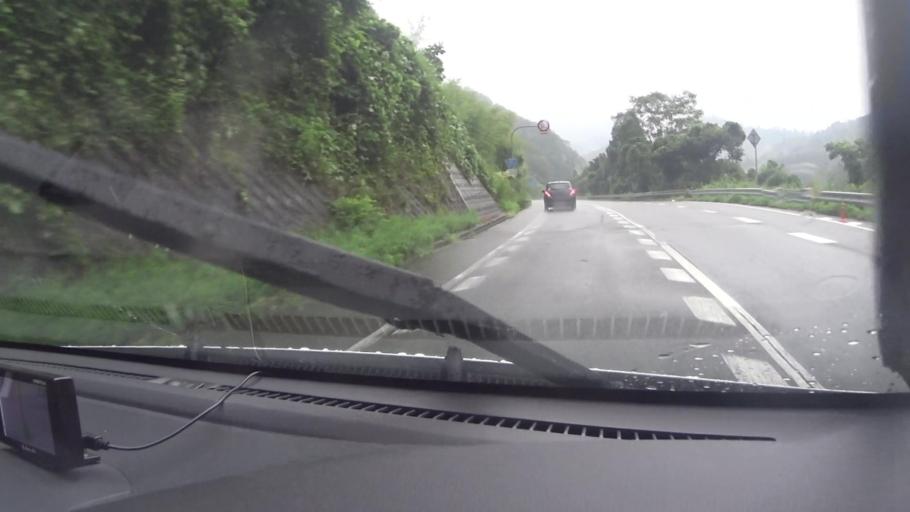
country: JP
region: Kyoto
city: Ayabe
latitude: 35.2678
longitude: 135.2710
